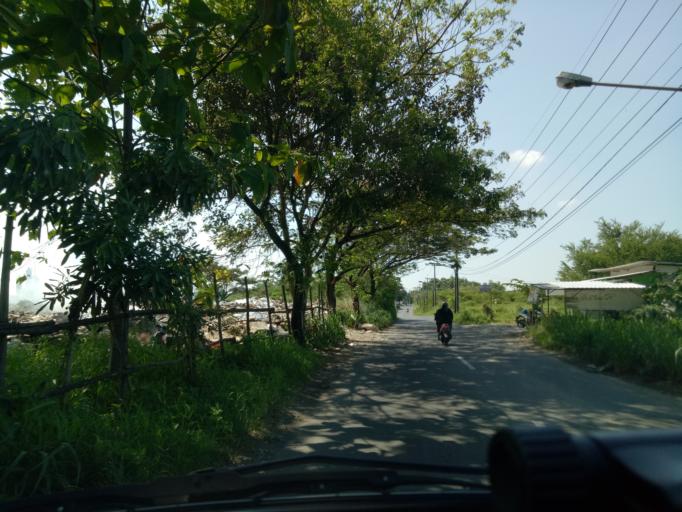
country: ID
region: East Java
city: Driyorejo
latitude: -7.2847
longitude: 112.6356
